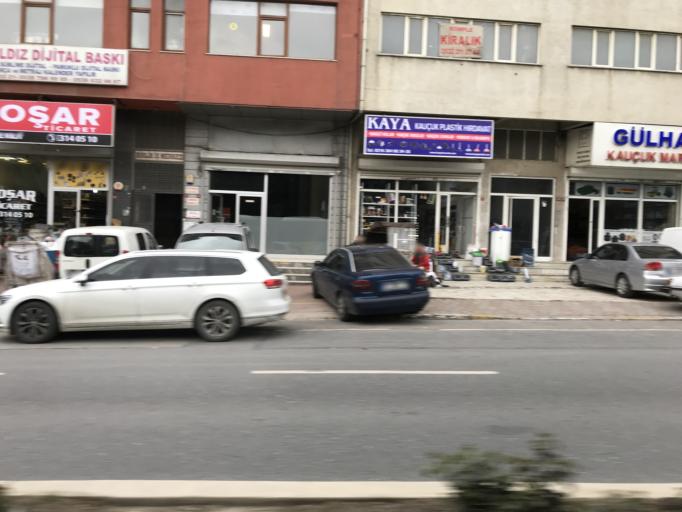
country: TR
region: Istanbul
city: Umraniye
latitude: 41.0106
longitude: 29.1644
